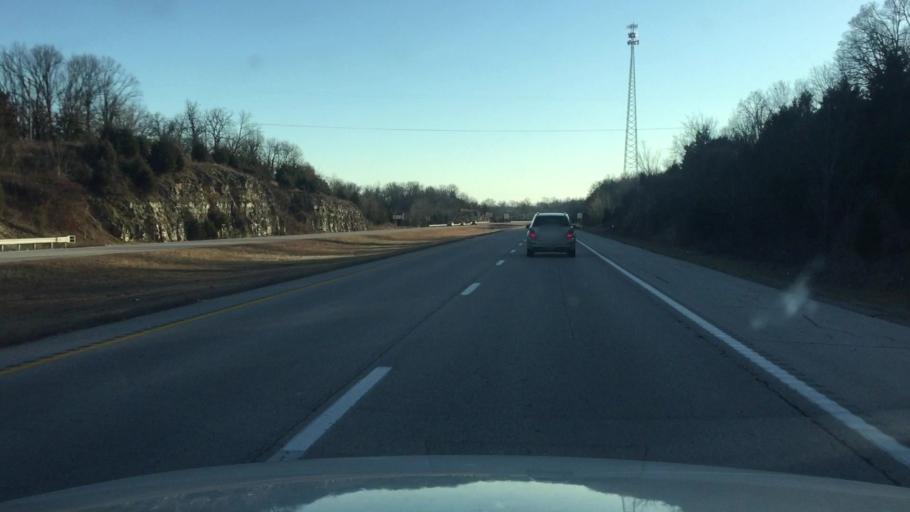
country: US
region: Missouri
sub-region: Cole County
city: Wardsville
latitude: 38.4824
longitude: -92.2728
